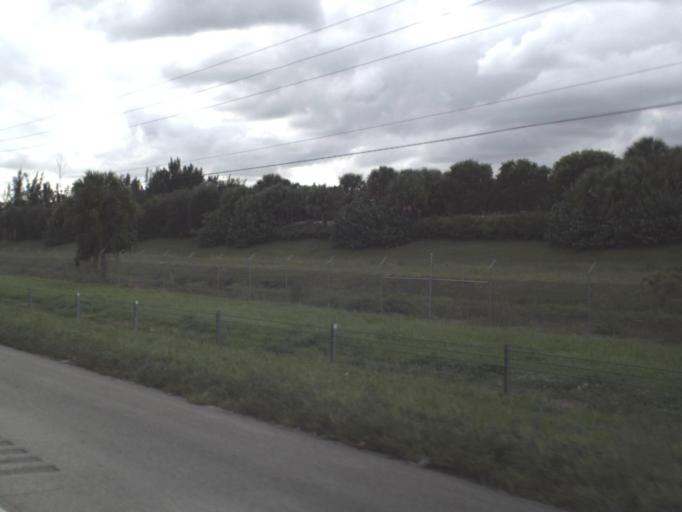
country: US
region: Florida
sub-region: Palm Beach County
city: Greenacres City
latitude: 26.6419
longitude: -80.1744
